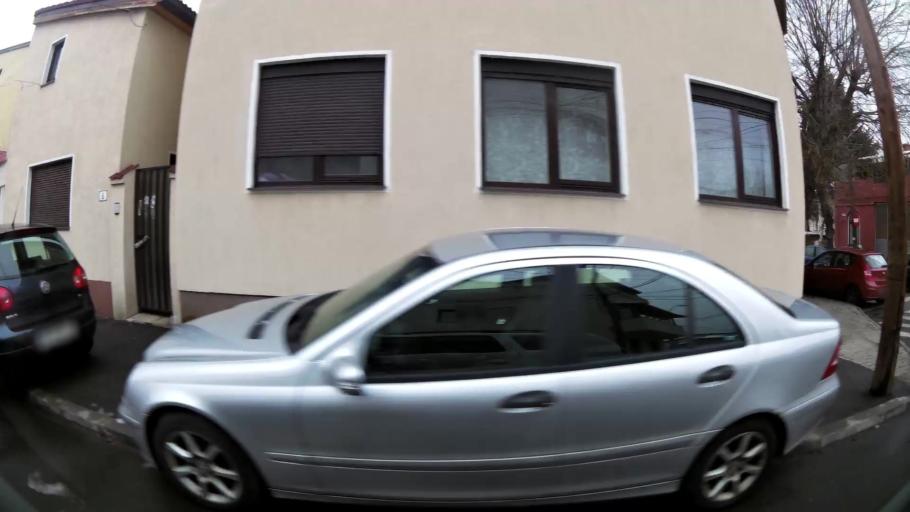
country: RO
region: Bucuresti
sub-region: Municipiul Bucuresti
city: Bucuresti
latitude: 44.4609
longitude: 26.0685
